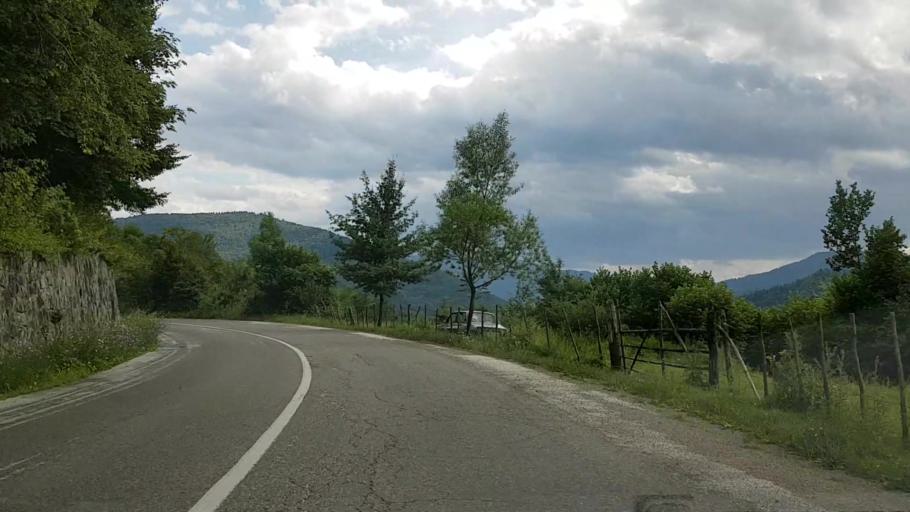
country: RO
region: Neamt
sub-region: Comuna Pangarati
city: Pangarati
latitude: 46.9612
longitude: 26.1223
